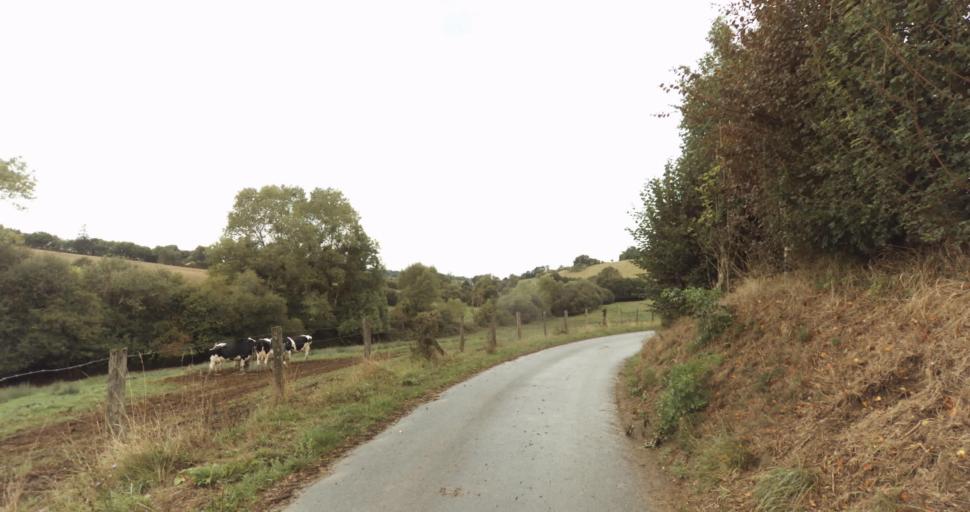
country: FR
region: Lower Normandy
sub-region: Departement de l'Orne
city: Vimoutiers
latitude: 48.8542
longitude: 0.2379
